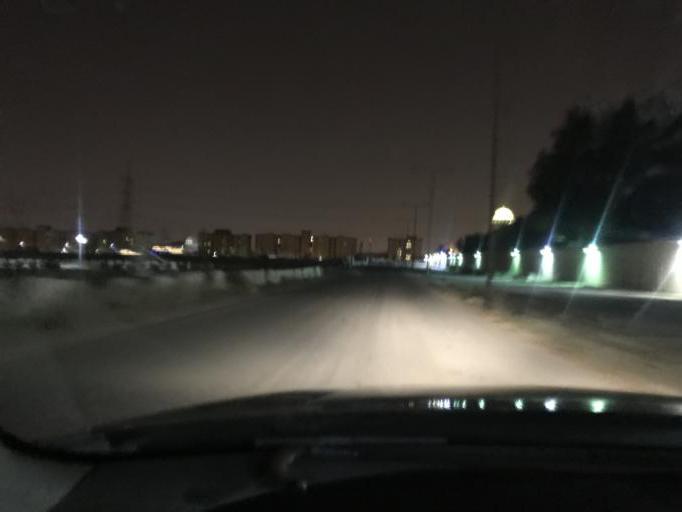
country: SA
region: Ar Riyad
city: Riyadh
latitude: 24.8135
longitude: 46.7167
